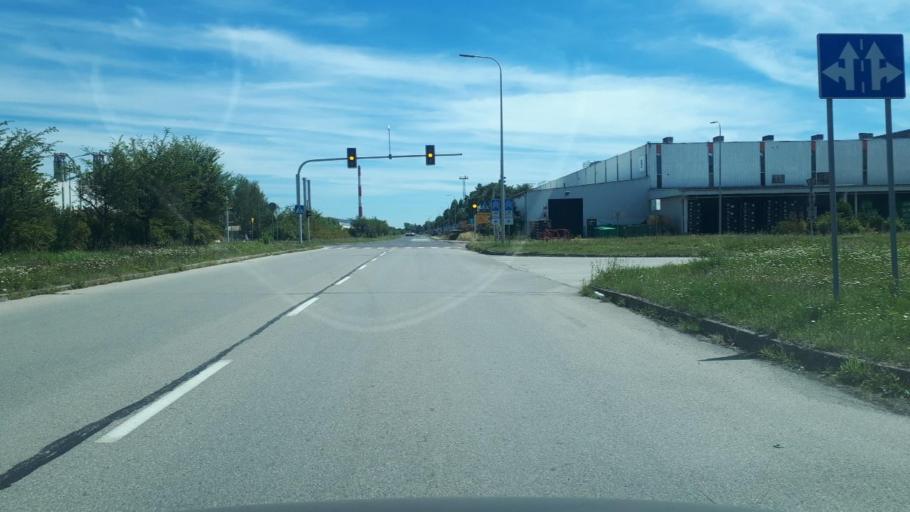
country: PL
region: Silesian Voivodeship
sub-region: Powiat bierunsko-ledzinski
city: Bierun
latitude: 50.1051
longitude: 19.0660
